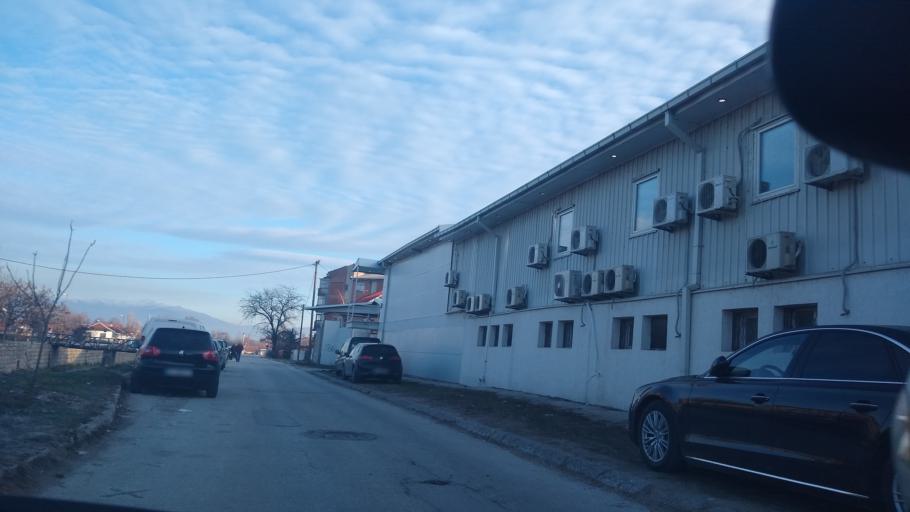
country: MK
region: Bitola
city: Bitola
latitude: 41.0299
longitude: 21.3454
